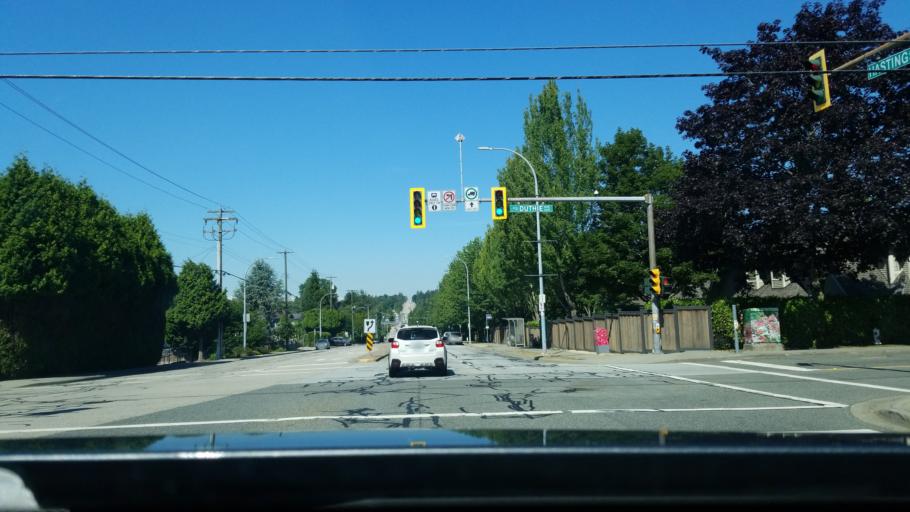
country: CA
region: British Columbia
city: Burnaby
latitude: 49.2804
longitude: -122.9531
